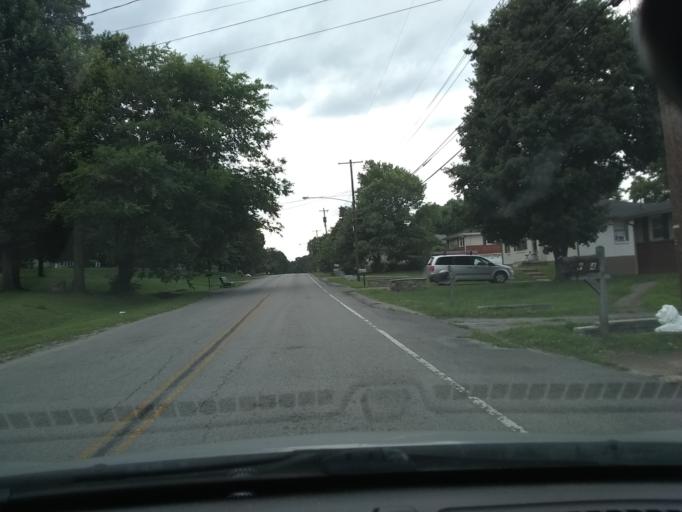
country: US
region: Tennessee
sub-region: Davidson County
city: Oak Hill
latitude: 36.1194
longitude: -86.7052
